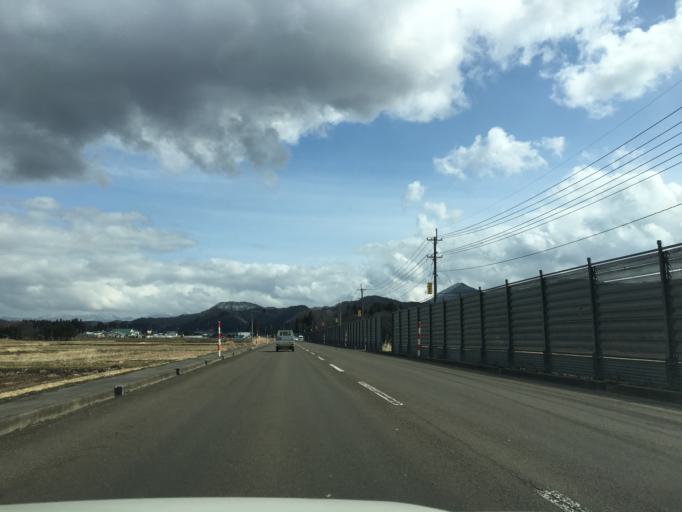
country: JP
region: Akita
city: Odate
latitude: 40.2167
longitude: 140.6178
